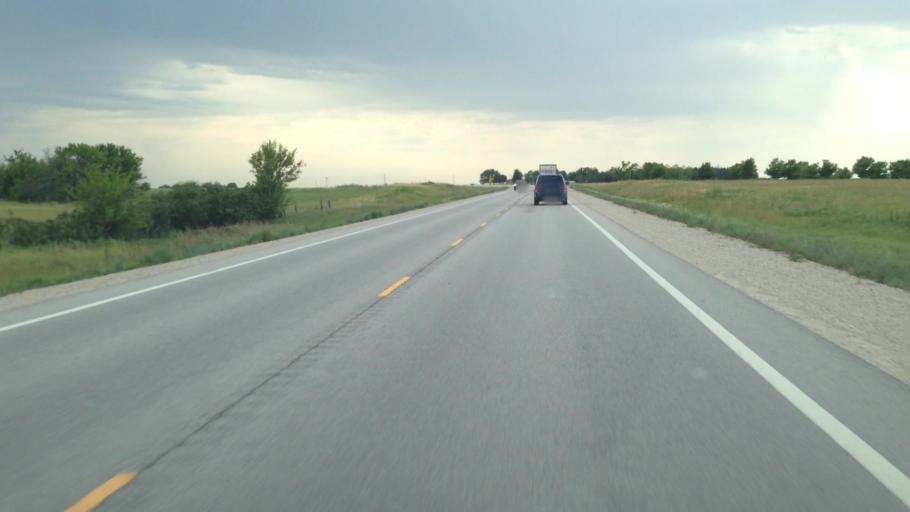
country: US
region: Kansas
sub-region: Coffey County
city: Burlington
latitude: 38.2948
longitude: -95.7328
